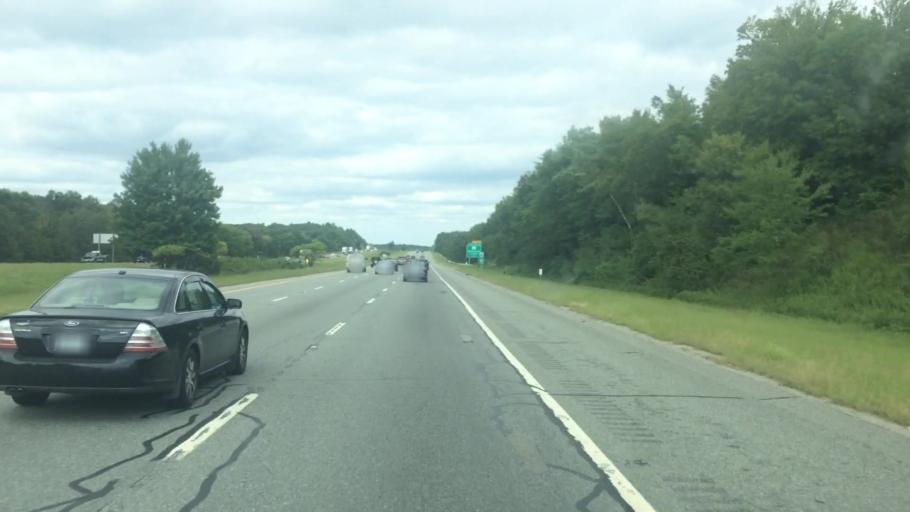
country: US
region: Rhode Island
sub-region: Providence County
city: Cumberland Hill
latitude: 41.9331
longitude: -71.4980
